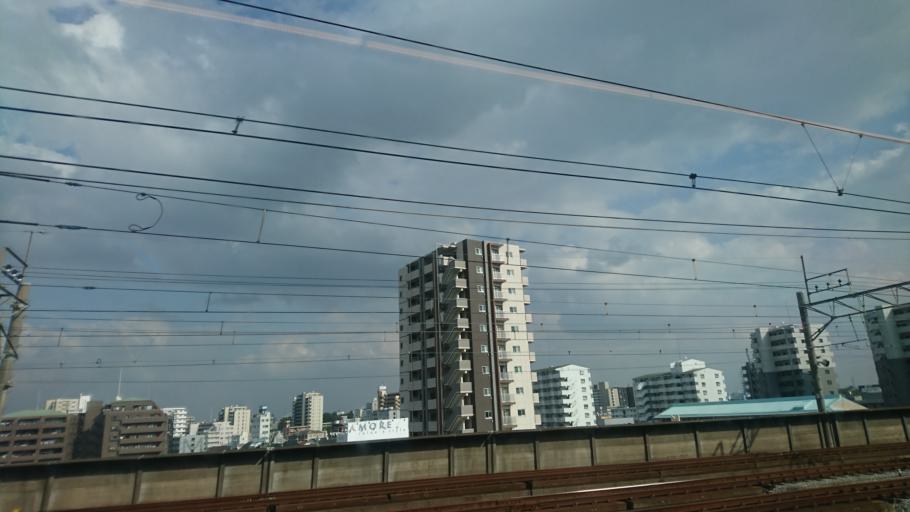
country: JP
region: Saitama
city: Yono
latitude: 35.8432
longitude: 139.6476
